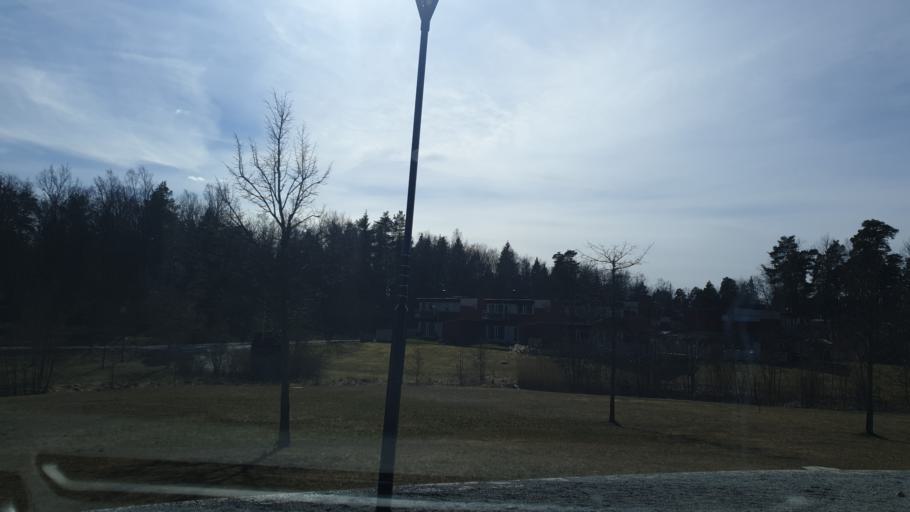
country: SE
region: Stockholm
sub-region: Solna Kommun
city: Rasunda
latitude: 59.3999
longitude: 17.9964
